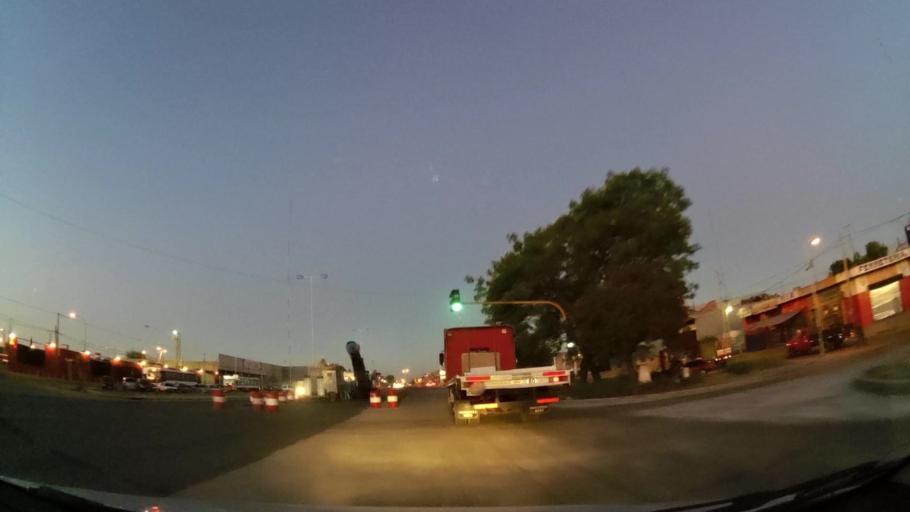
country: AR
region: Buenos Aires
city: San Justo
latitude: -34.7102
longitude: -58.5887
